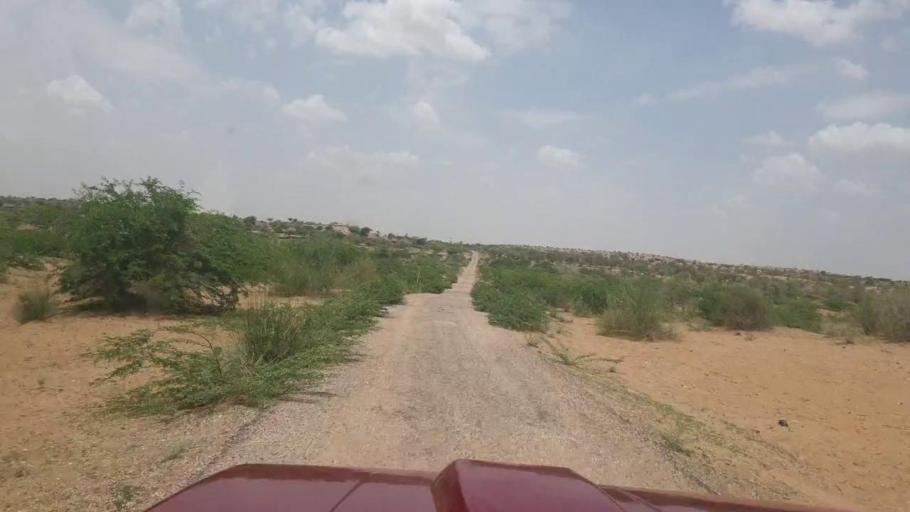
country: PK
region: Sindh
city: Islamkot
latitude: 25.2283
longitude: 70.5017
